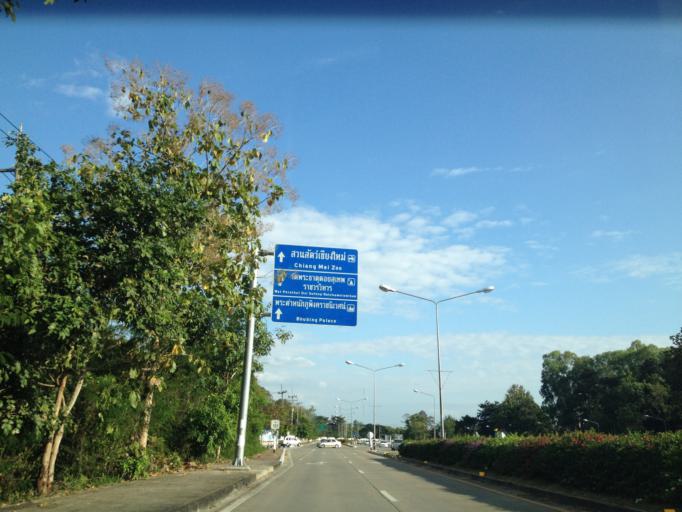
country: TH
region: Chiang Mai
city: Chiang Mai
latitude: 18.8441
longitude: 98.9620
